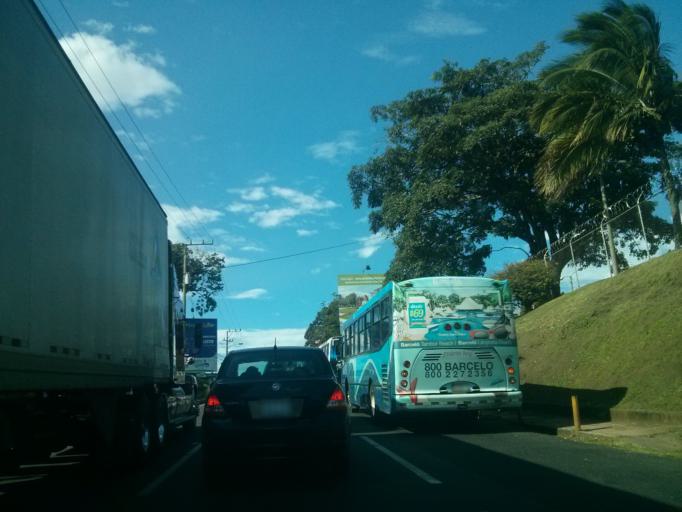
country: CR
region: San Jose
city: Colima
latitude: 9.9650
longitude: -84.1125
